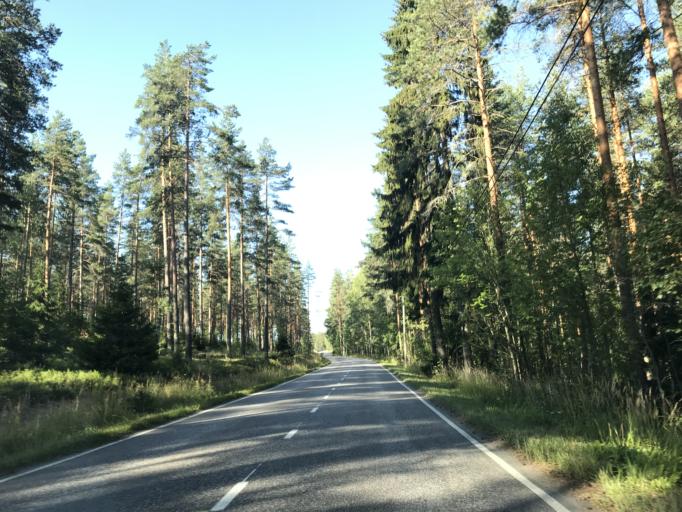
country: FI
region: Uusimaa
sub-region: Helsinki
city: Lohja
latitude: 60.2801
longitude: 24.1298
